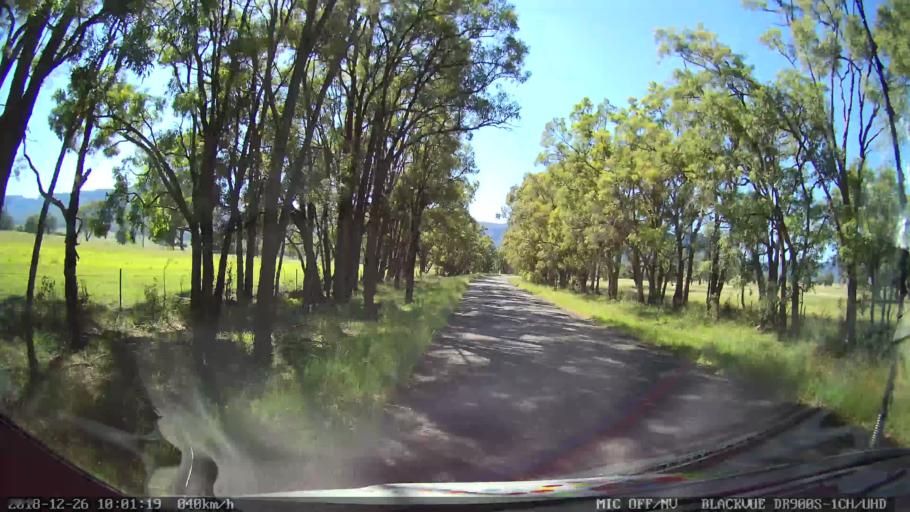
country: AU
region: New South Wales
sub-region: Mid-Western Regional
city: Kandos
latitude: -33.0468
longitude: 150.2208
